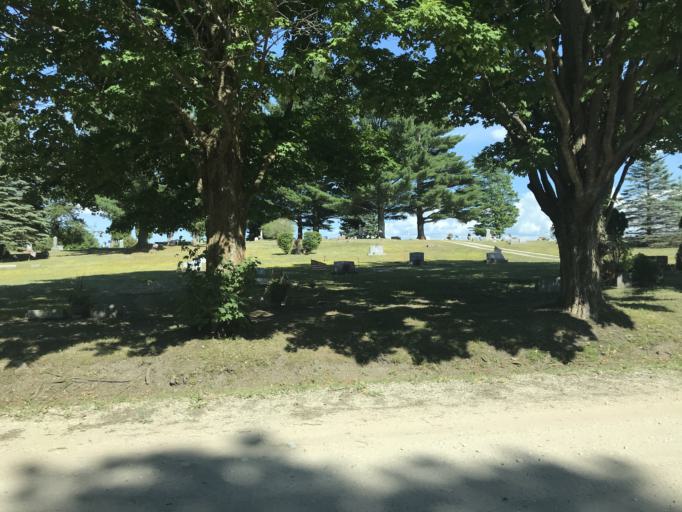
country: US
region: Michigan
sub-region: Cheboygan County
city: Cheboygan
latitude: 45.6210
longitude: -84.6507
